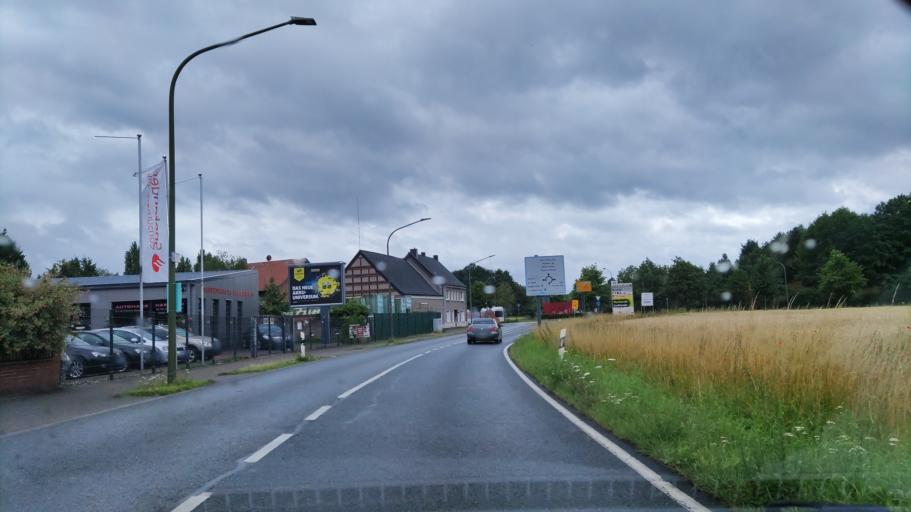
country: DE
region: North Rhine-Westphalia
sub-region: Regierungsbezirk Arnsberg
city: Hamm
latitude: 51.7110
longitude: 7.8359
